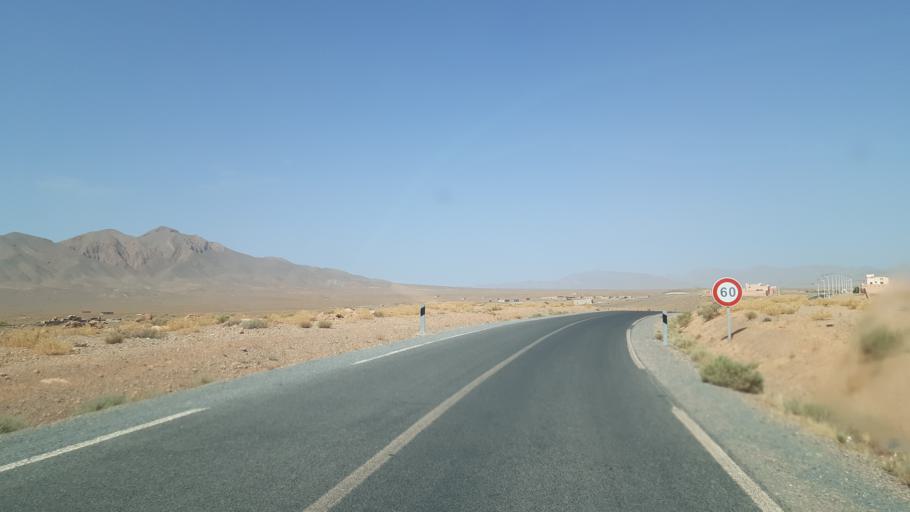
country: MA
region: Meknes-Tafilalet
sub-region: Errachidia
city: Amouguer
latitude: 32.2220
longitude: -4.6747
